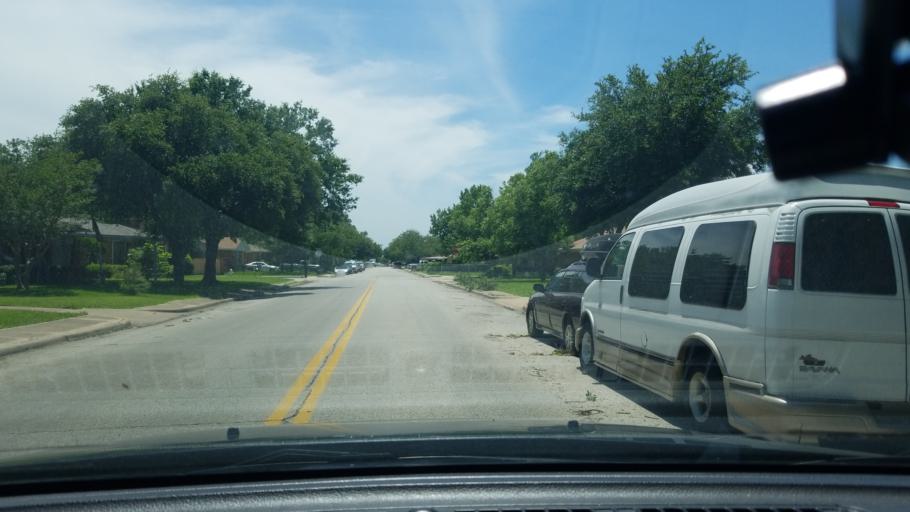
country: US
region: Texas
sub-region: Dallas County
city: Mesquite
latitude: 32.7889
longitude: -96.6131
